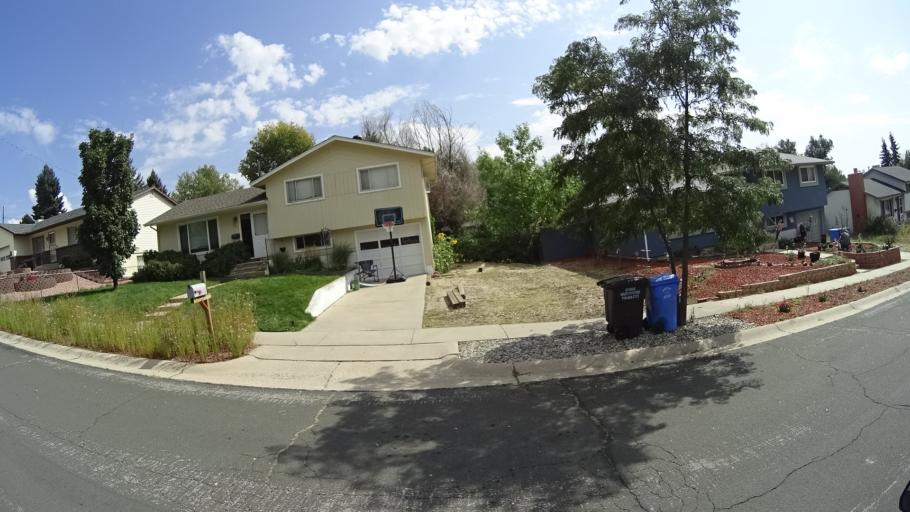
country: US
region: Colorado
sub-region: El Paso County
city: Colorado Springs
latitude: 38.8610
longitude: -104.7706
